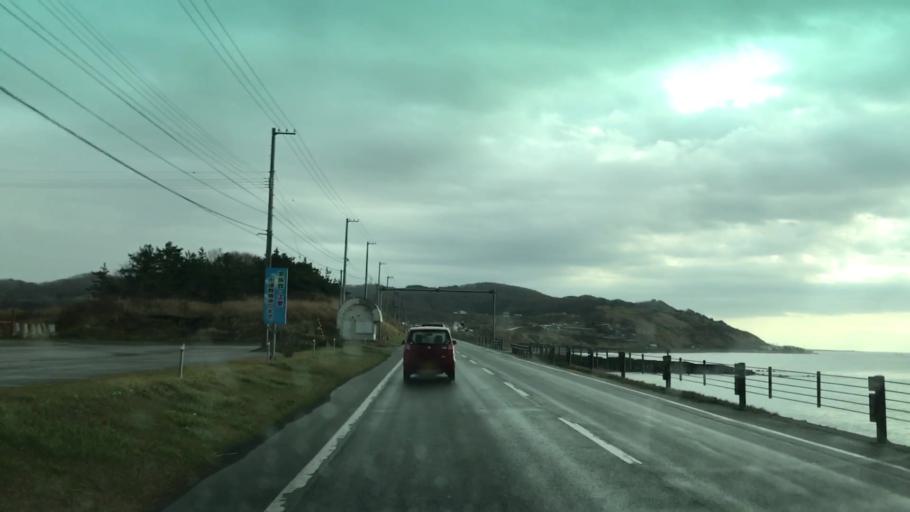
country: JP
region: Hokkaido
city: Shizunai-furukawacho
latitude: 42.1865
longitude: 142.7143
